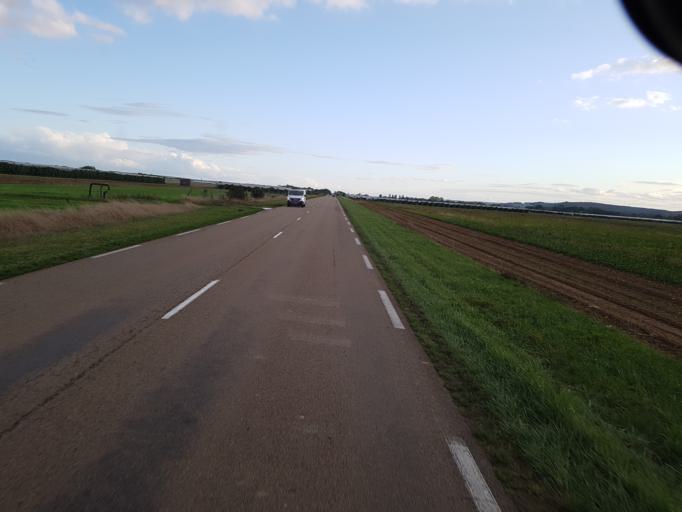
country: FR
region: Bourgogne
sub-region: Departement de l'Yonne
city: Saint-Clement
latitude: 48.2538
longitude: 3.2845
